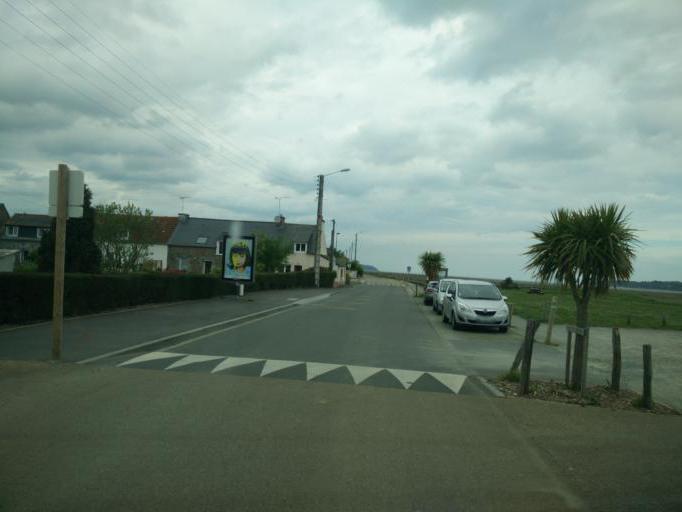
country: FR
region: Brittany
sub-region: Departement des Cotes-d'Armor
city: Yffiniac
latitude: 48.4930
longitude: -2.6864
